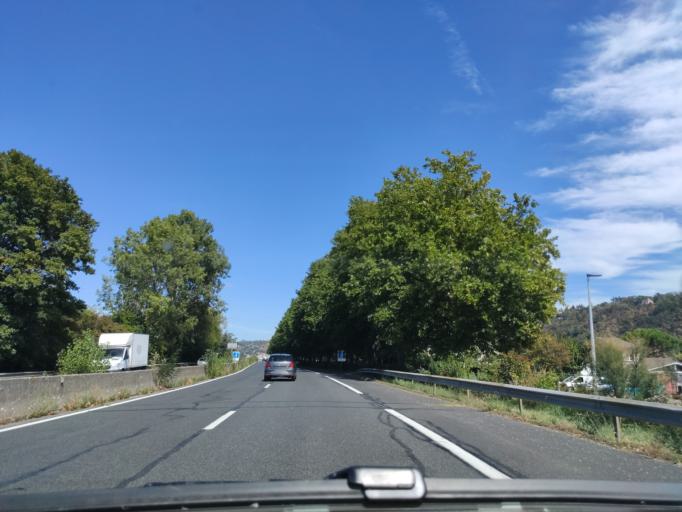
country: FR
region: Rhone-Alpes
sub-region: Departement du Rhone
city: Saint-Cyr-sur-le-Rhone
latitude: 45.5061
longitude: 4.8516
